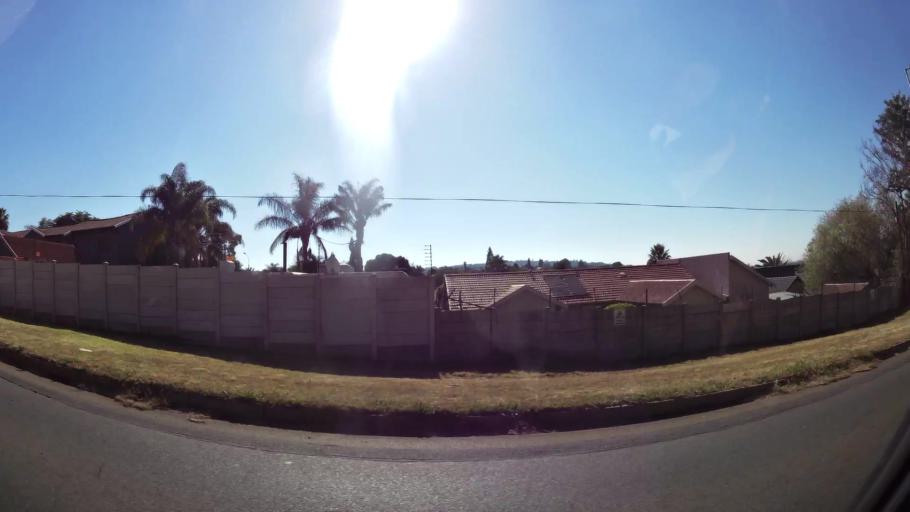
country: ZA
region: Gauteng
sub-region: City of Johannesburg Metropolitan Municipality
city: Roodepoort
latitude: -26.1208
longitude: 27.8608
